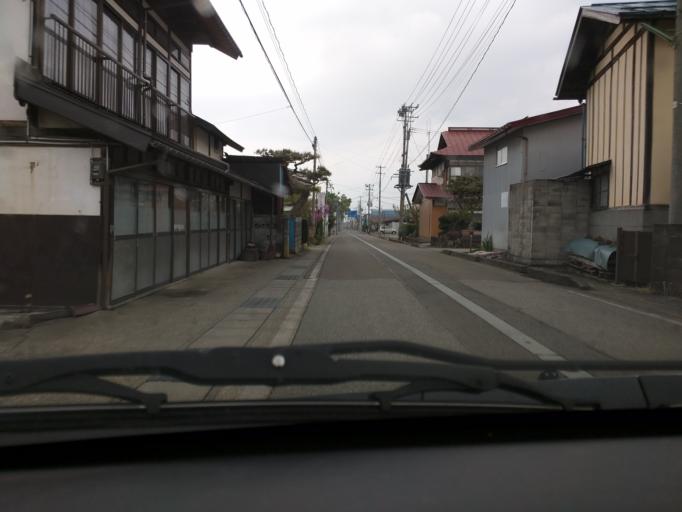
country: JP
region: Fukushima
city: Kitakata
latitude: 37.4524
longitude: 139.8348
